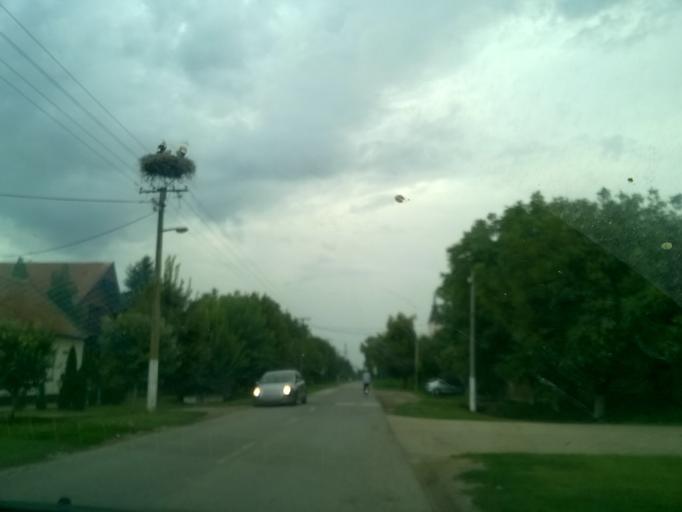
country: RS
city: Tomasevac
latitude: 45.2655
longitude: 20.6194
